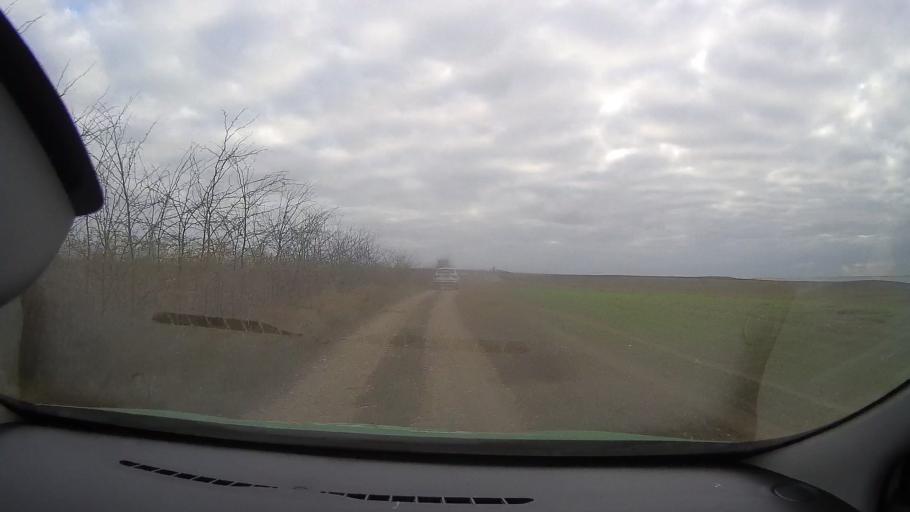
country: RO
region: Tulcea
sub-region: Comuna Jurilovca
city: Jurilovca
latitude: 44.7695
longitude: 28.9103
